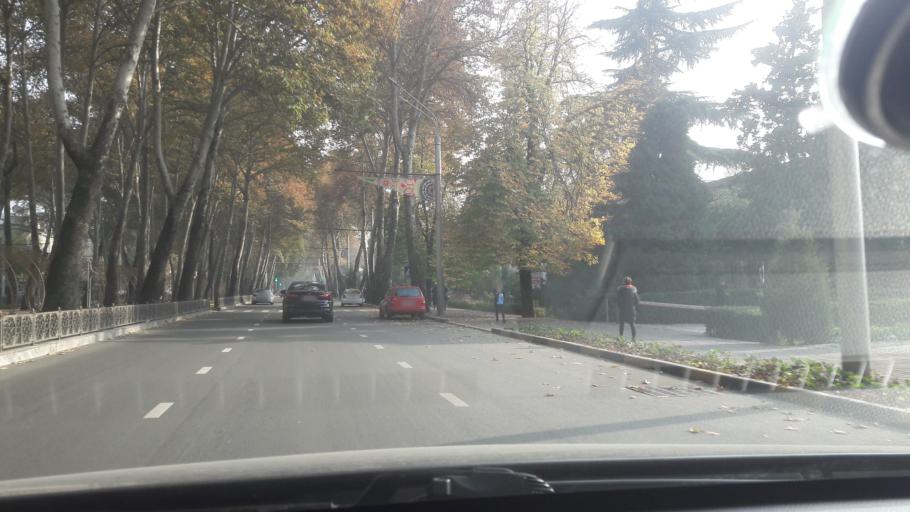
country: TJ
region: Dushanbe
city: Dushanbe
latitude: 38.5693
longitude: 68.7913
